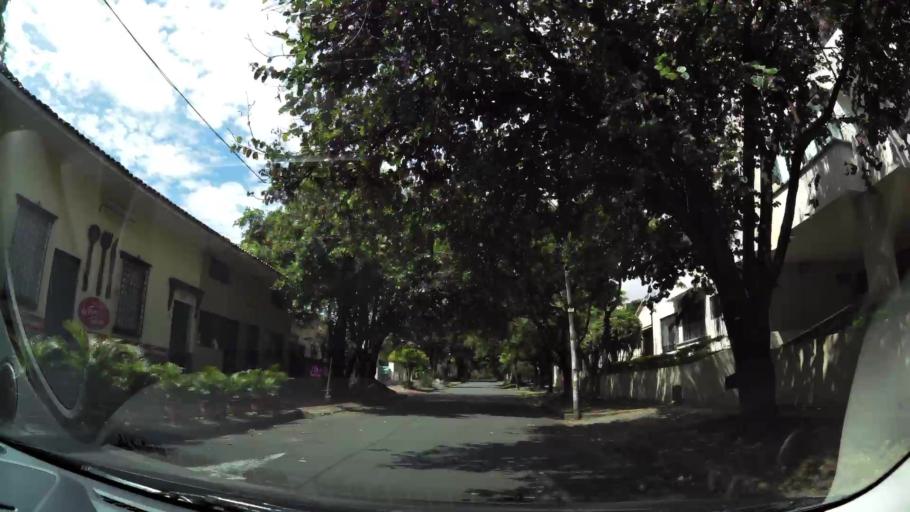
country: CO
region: Valle del Cauca
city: Cali
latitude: 3.4336
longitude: -76.5450
